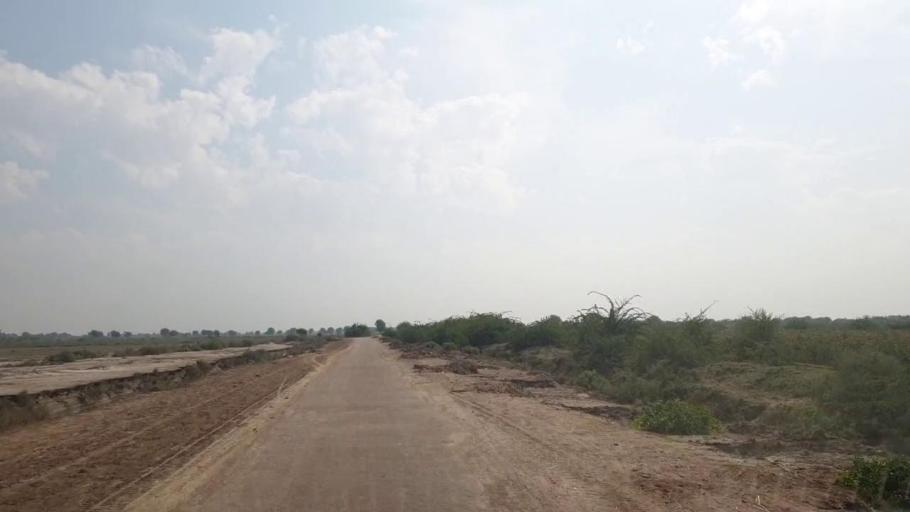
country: PK
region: Sindh
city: Rajo Khanani
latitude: 24.9657
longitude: 69.0110
